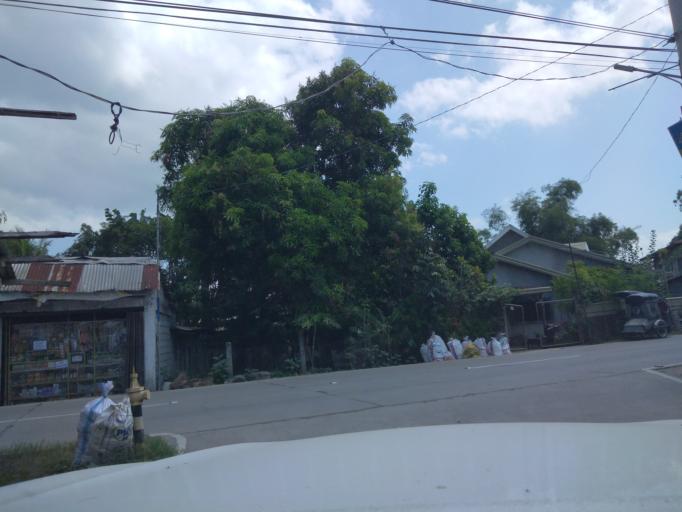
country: PH
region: Central Luzon
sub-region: Province of Pampanga
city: Lourdes
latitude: 15.0191
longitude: 120.8503
